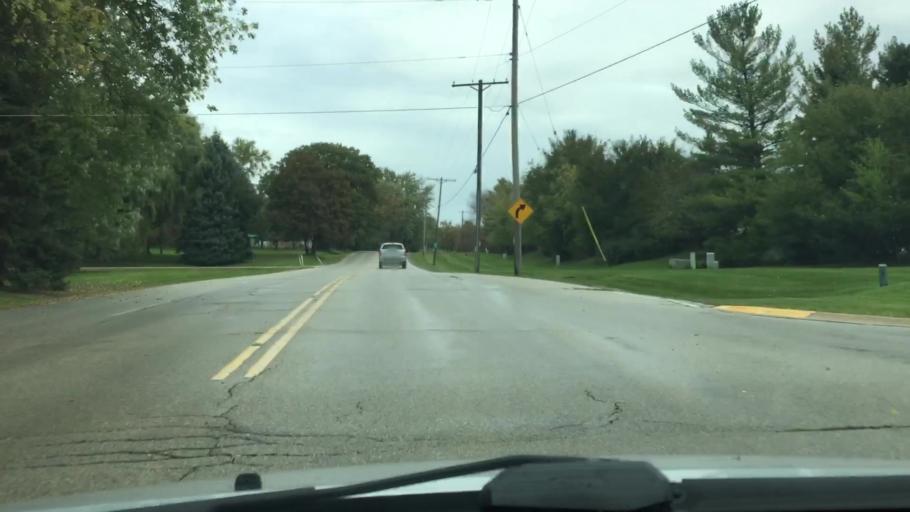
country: US
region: Wisconsin
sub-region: Waukesha County
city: Pewaukee
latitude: 43.0598
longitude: -88.2828
